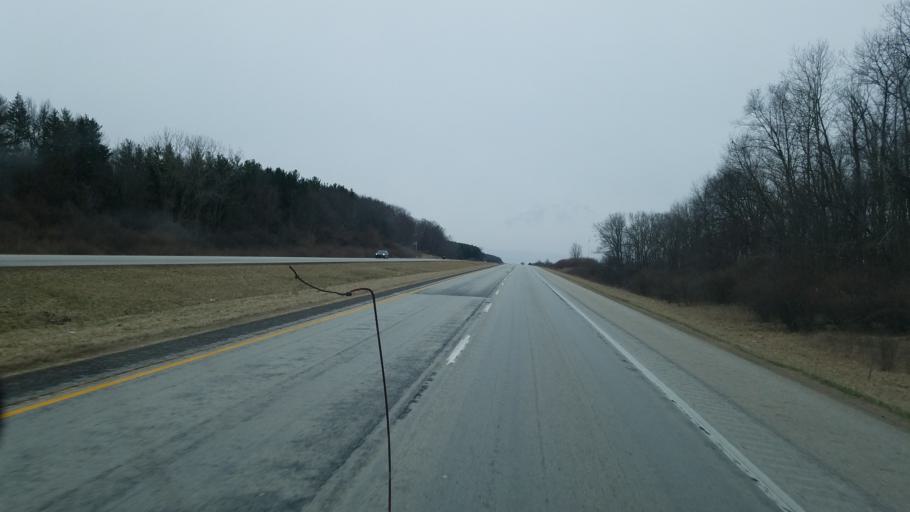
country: US
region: Indiana
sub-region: Fulton County
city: Rochester
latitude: 41.1324
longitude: -86.2400
